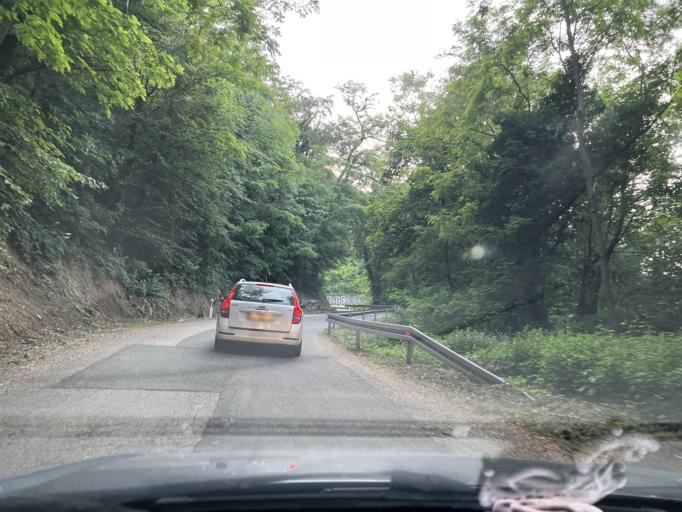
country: HR
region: Primorsko-Goranska
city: Marcelji
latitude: 45.3977
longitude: 14.4170
